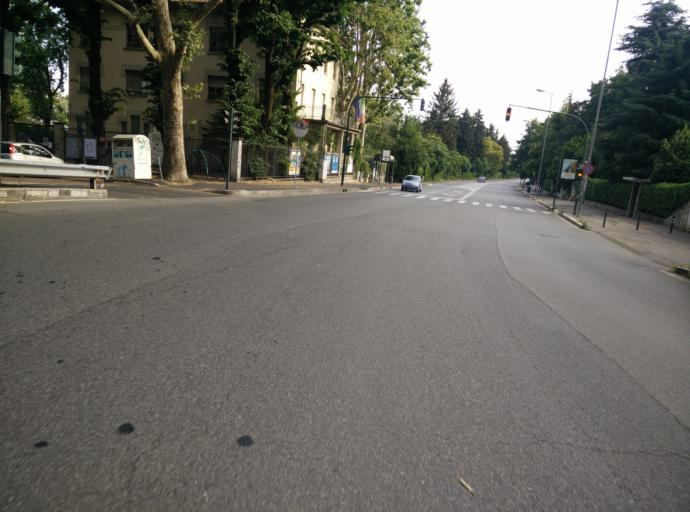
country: IT
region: Piedmont
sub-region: Provincia di Torino
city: Moncalieri
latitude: 45.0249
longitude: 7.6760
